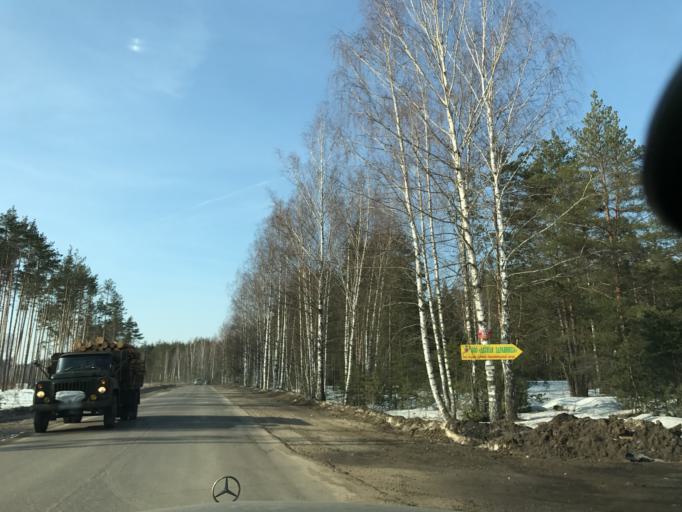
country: RU
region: Nizjnij Novgorod
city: Taremskoye
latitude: 56.0097
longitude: 42.9806
